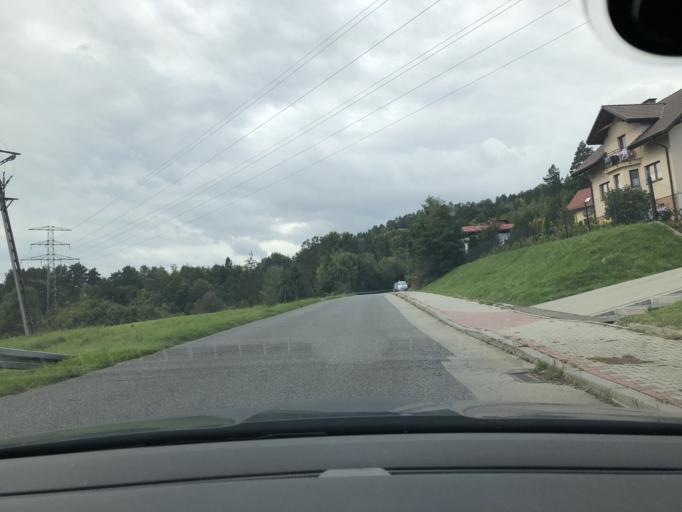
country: PL
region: Silesian Voivodeship
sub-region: Powiat zywiecki
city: Zarzecze
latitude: 49.7283
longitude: 19.1903
